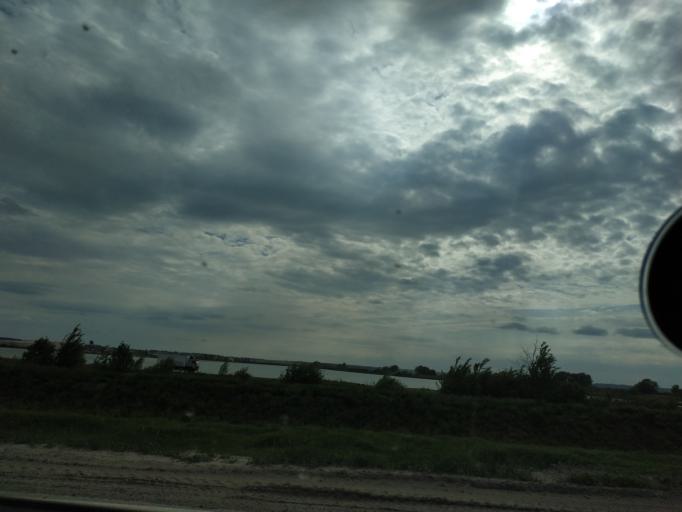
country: RU
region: Moskovskaya
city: Malyshevo
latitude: 55.5112
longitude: 38.2813
